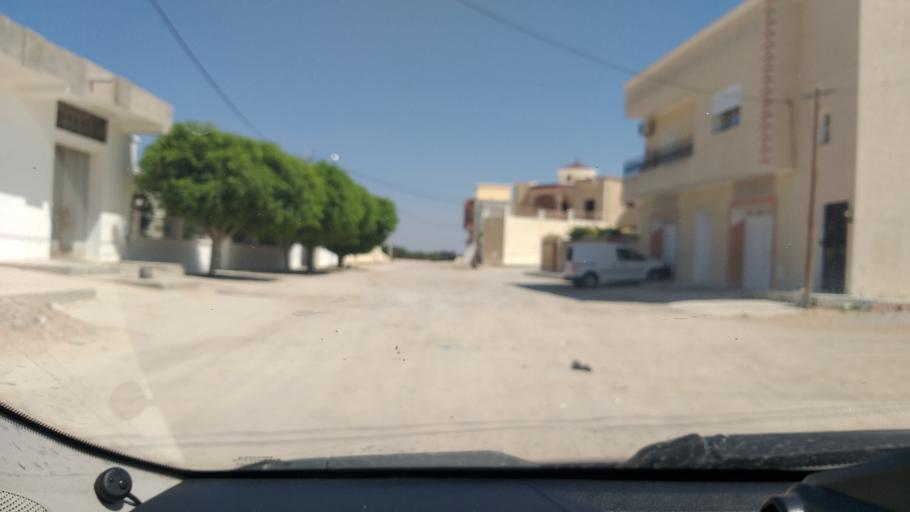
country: TN
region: Al Mahdiyah
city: El Jem
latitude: 35.2885
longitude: 10.7184
